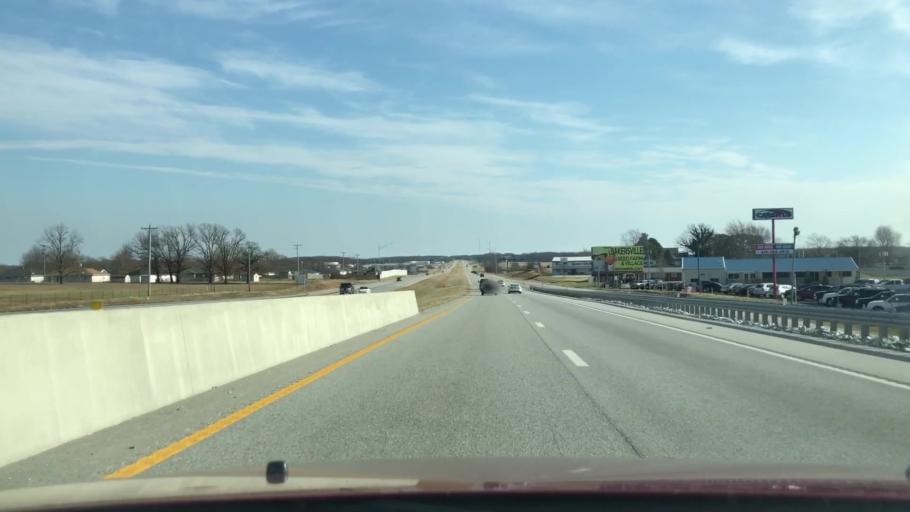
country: US
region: Missouri
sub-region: Webster County
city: Rogersville
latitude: 37.1109
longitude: -93.0548
